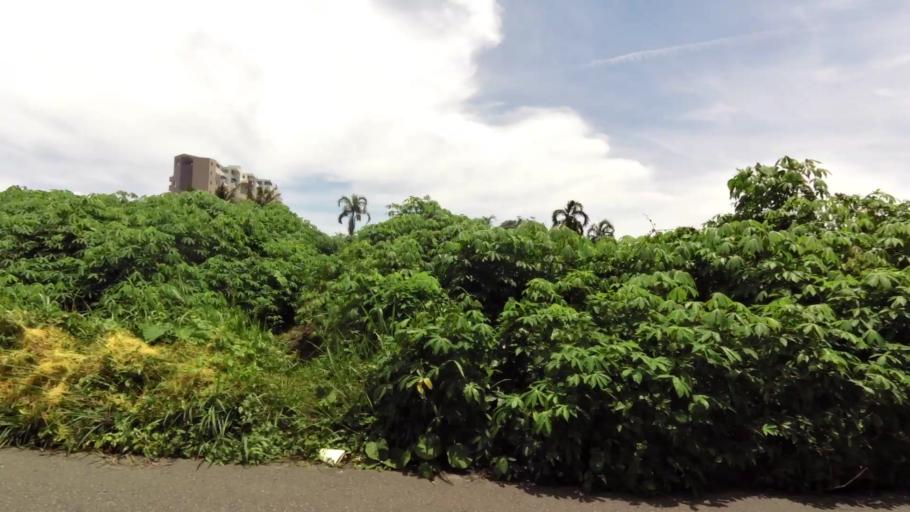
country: BN
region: Belait
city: Kuala Belait
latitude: 4.5931
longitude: 114.2466
